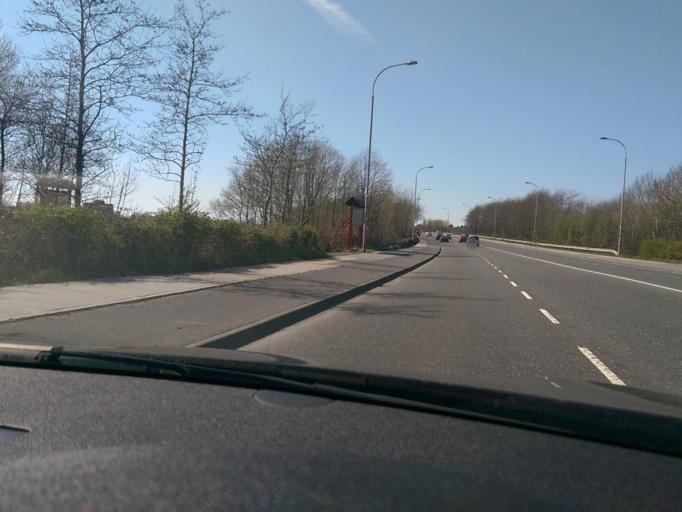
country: IE
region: Connaught
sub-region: County Galway
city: Gaillimh
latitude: 53.2828
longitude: -9.0539
